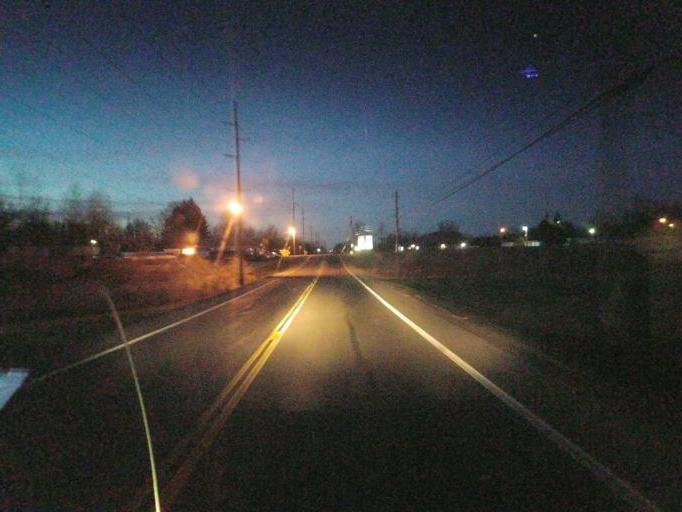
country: US
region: Ohio
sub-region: Logan County
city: Bellefontaine
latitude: 40.3860
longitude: -83.7529
